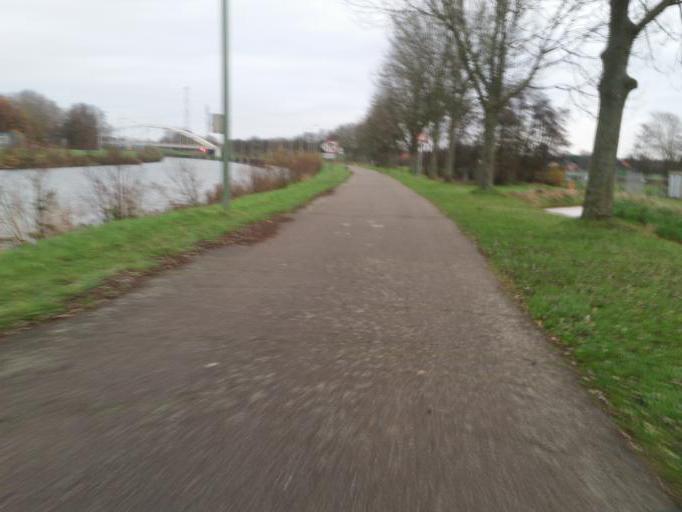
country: BE
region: Flanders
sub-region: Provincie Antwerpen
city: Nijlen
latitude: 51.1824
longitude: 4.6628
